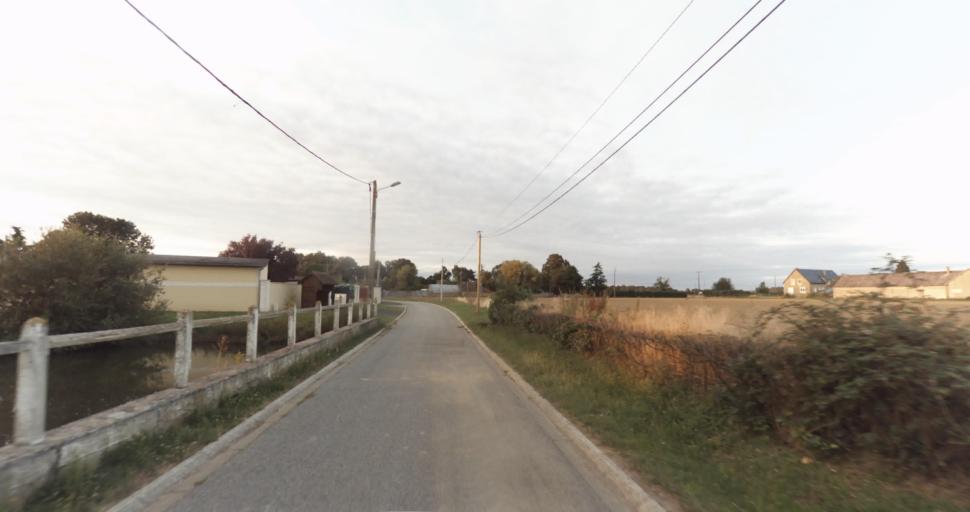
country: FR
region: Haute-Normandie
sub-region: Departement de l'Eure
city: La Madeleine-de-Nonancourt
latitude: 48.8733
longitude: 1.1853
